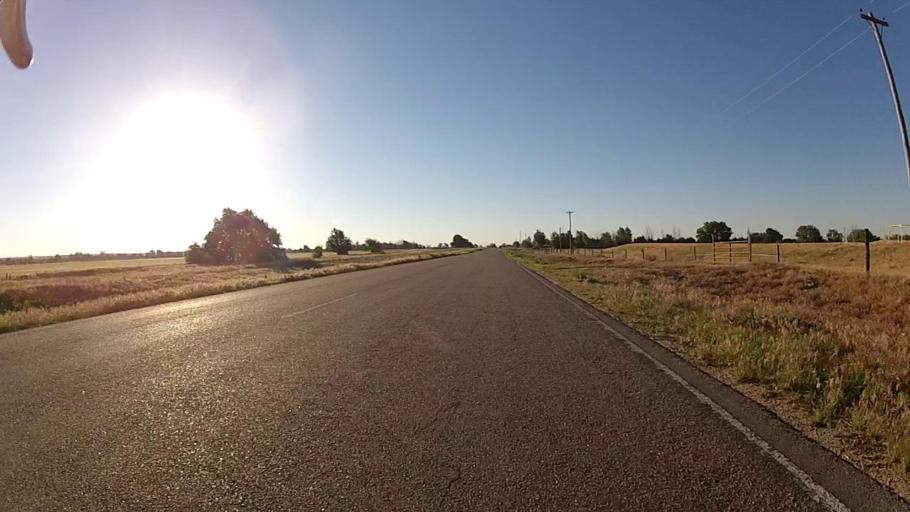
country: US
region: Kansas
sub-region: Ford County
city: Dodge City
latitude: 37.7096
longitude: -99.9150
